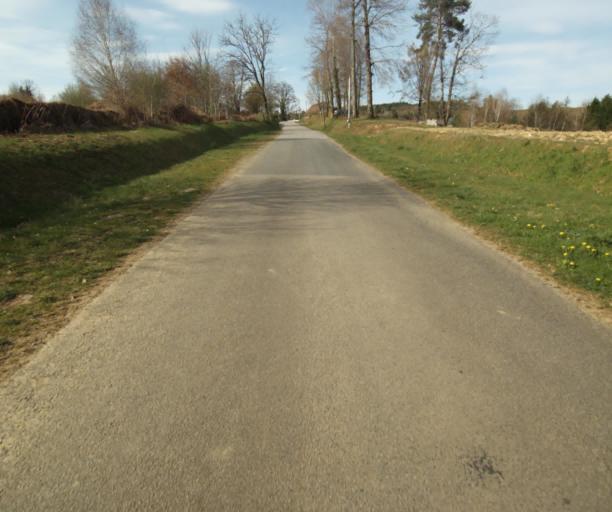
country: FR
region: Limousin
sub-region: Departement de la Correze
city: Naves
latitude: 45.3179
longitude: 1.7263
